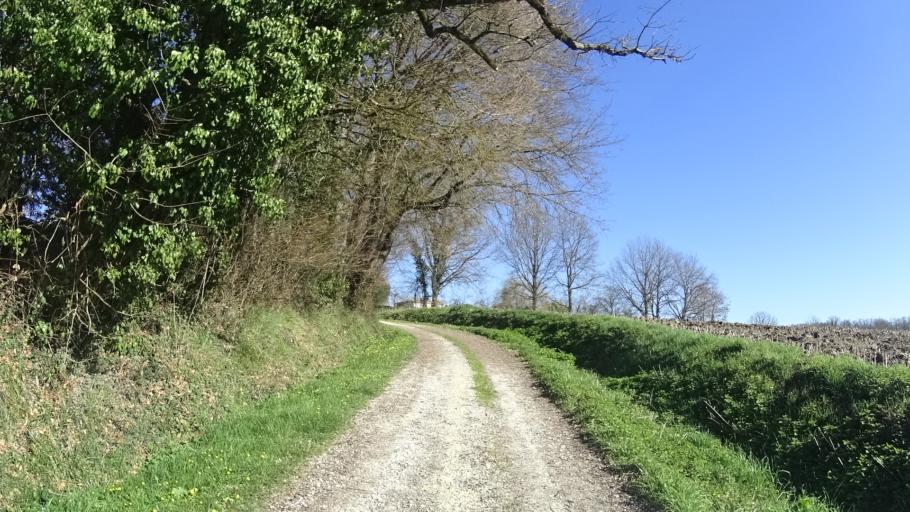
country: FR
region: Aquitaine
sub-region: Departement de la Dordogne
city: Saint-Aulaye
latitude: 45.2212
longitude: 0.1165
